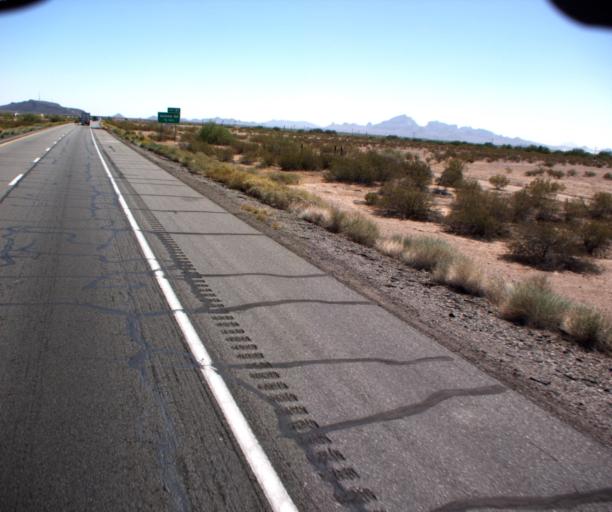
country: US
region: Arizona
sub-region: La Paz County
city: Salome
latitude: 33.5409
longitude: -113.1713
